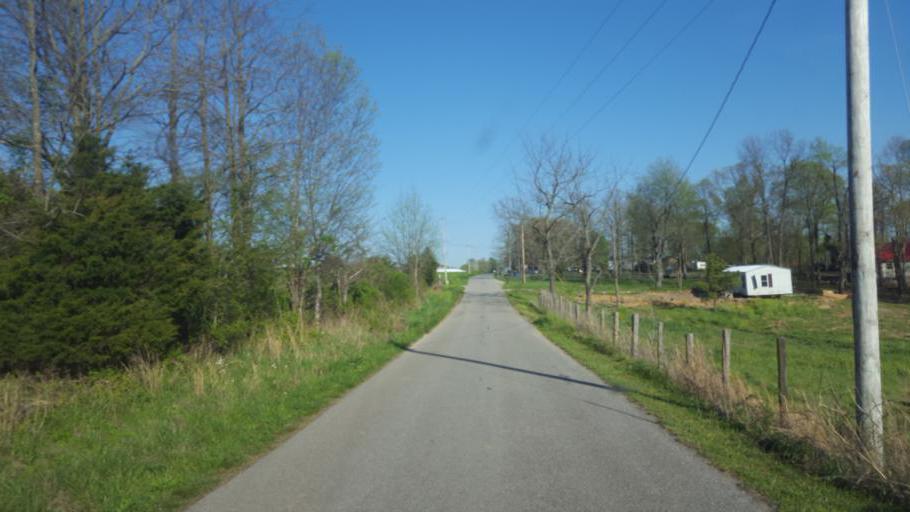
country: US
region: Kentucky
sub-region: Barren County
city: Cave City
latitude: 37.1732
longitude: -85.9933
